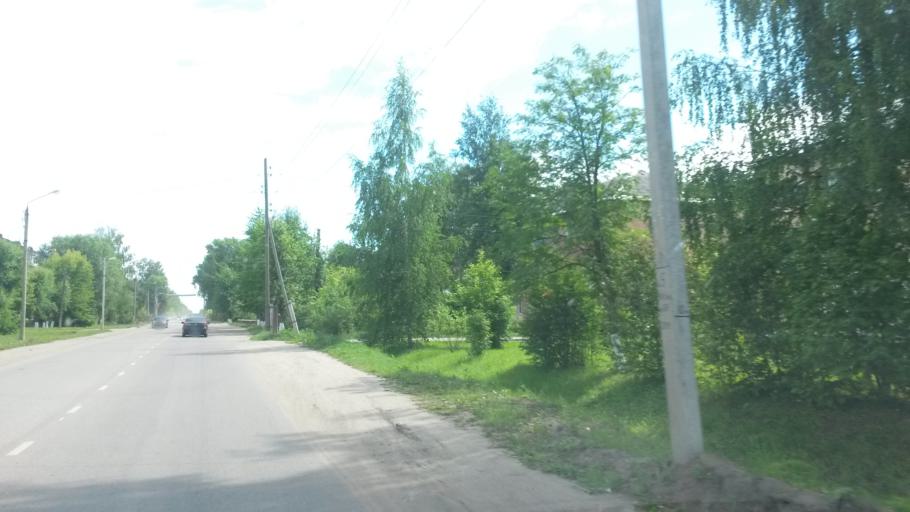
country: RU
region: Ivanovo
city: Zavolzhsk
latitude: 57.4940
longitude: 42.1350
